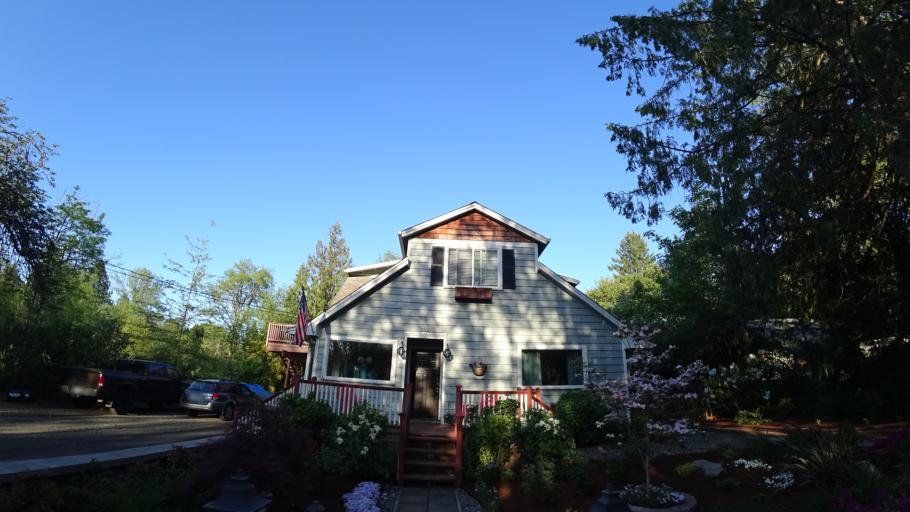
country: US
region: Oregon
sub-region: Washington County
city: West Slope
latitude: 45.4926
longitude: -122.7692
